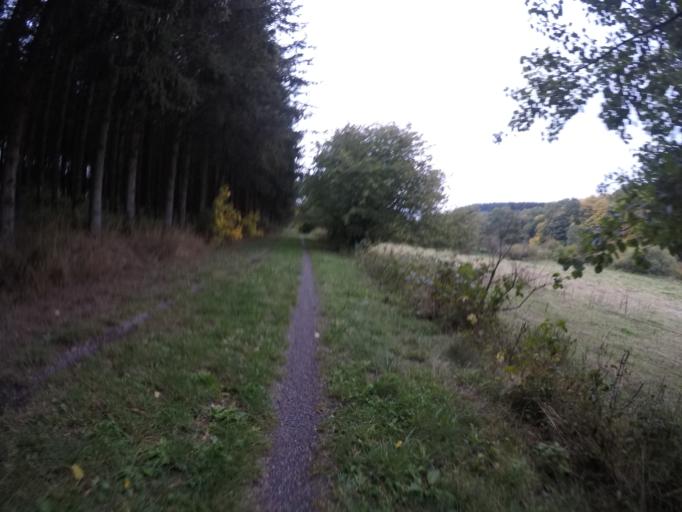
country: BE
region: Wallonia
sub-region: Province du Luxembourg
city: Fauvillers
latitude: 49.8638
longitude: 5.6914
